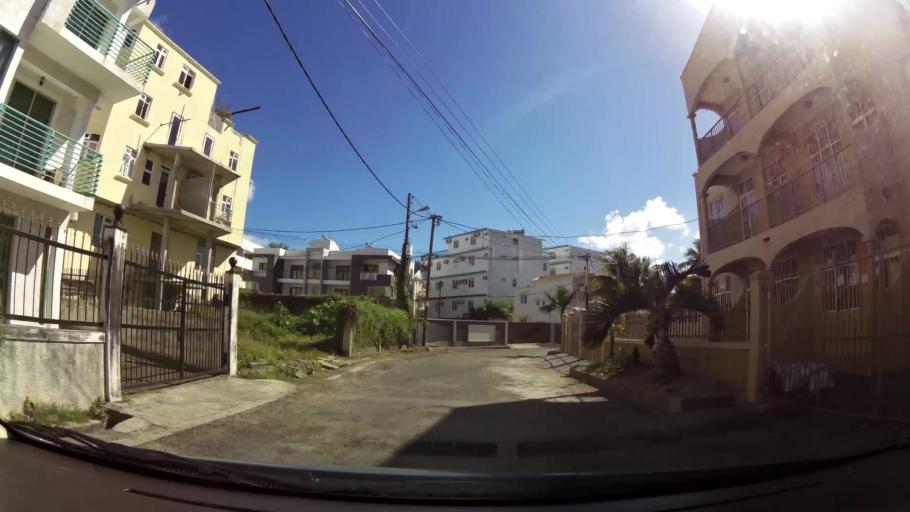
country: MU
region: Black River
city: Flic en Flac
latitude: -20.2941
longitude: 57.3649
